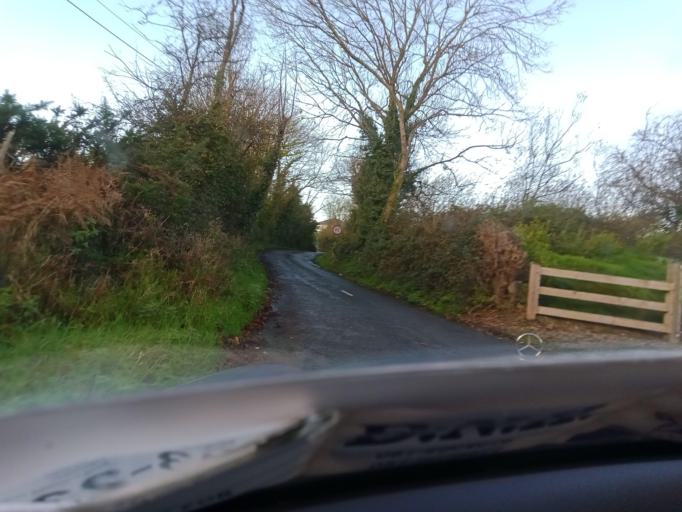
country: IE
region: Munster
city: Carrick-on-Suir
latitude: 52.3319
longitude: -7.4084
